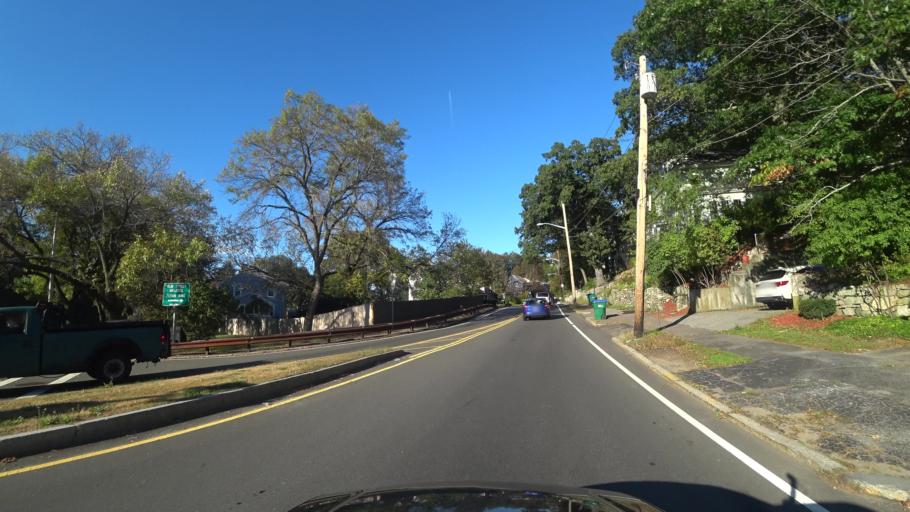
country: US
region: Massachusetts
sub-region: Middlesex County
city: Medford
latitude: 42.4362
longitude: -71.1018
